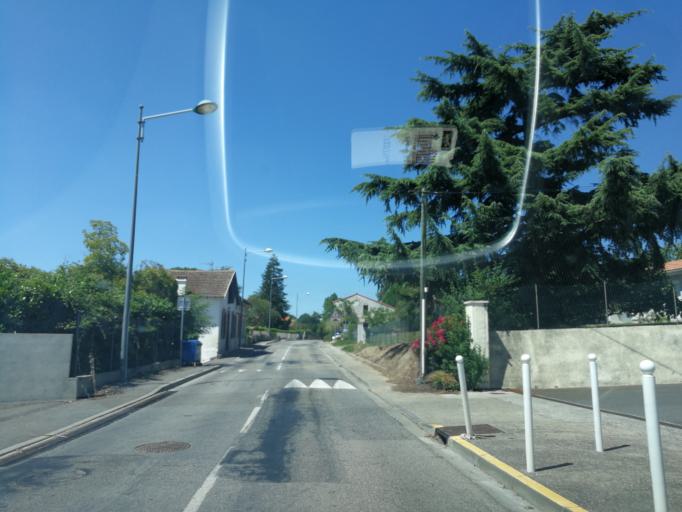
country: FR
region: Midi-Pyrenees
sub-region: Departement de la Haute-Garonne
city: Balma
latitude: 43.6212
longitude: 1.5013
